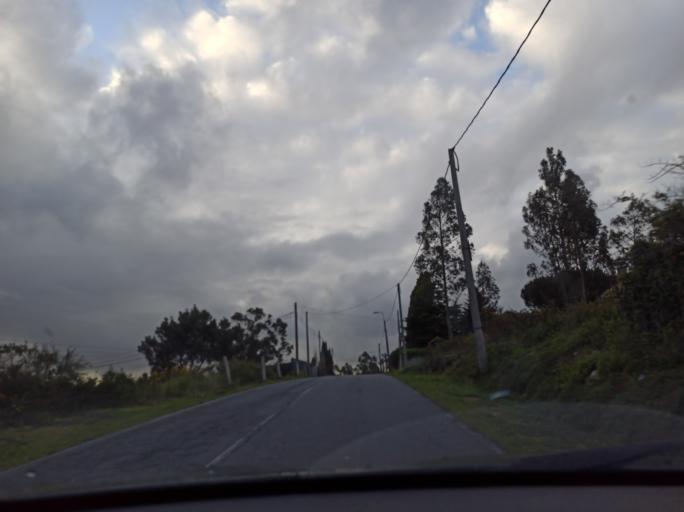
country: ES
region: Galicia
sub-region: Provincia da Coruna
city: Culleredo
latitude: 43.2973
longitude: -8.4309
